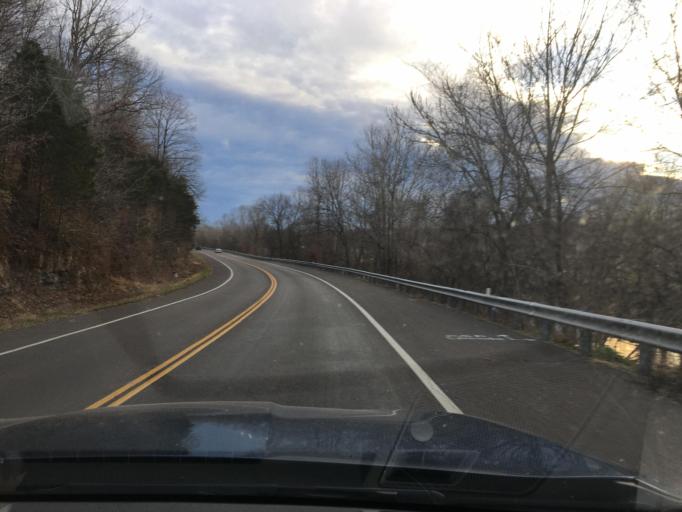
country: US
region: Missouri
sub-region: Jefferson County
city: De Soto
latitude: 38.1322
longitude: -90.5540
